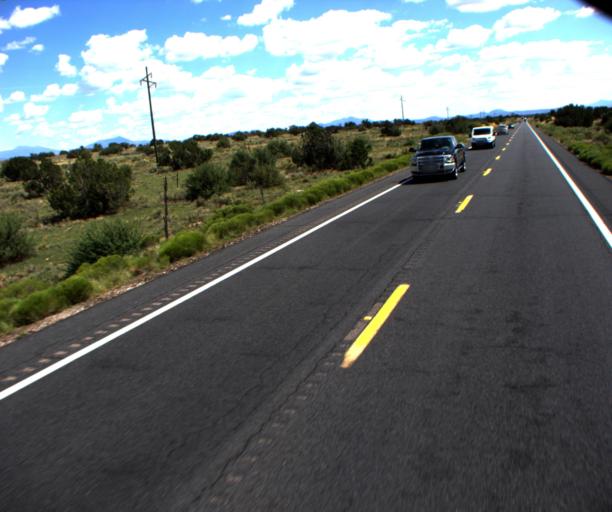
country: US
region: Arizona
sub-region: Coconino County
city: Grand Canyon Village
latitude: 35.7209
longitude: -112.1312
